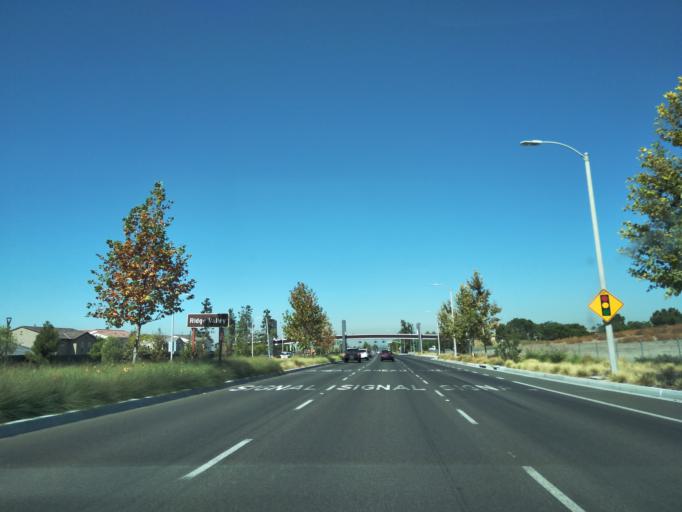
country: US
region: California
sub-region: Orange County
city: Lake Forest
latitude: 33.6925
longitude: -117.7294
